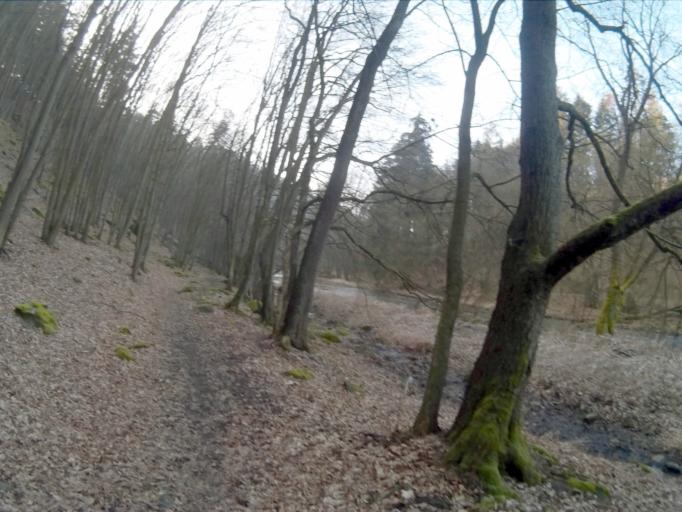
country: CZ
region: Vysocina
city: Namest' nad Oslavou
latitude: 49.1821
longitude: 16.1606
